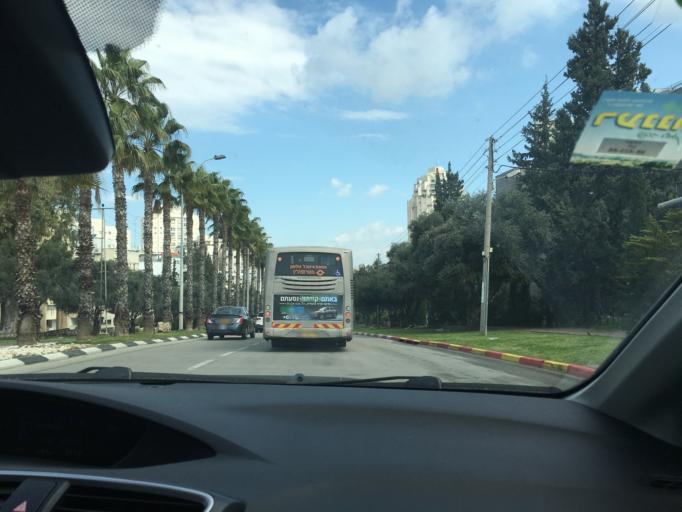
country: IL
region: Tel Aviv
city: Ramat HaSharon
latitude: 32.1489
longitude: 34.8404
